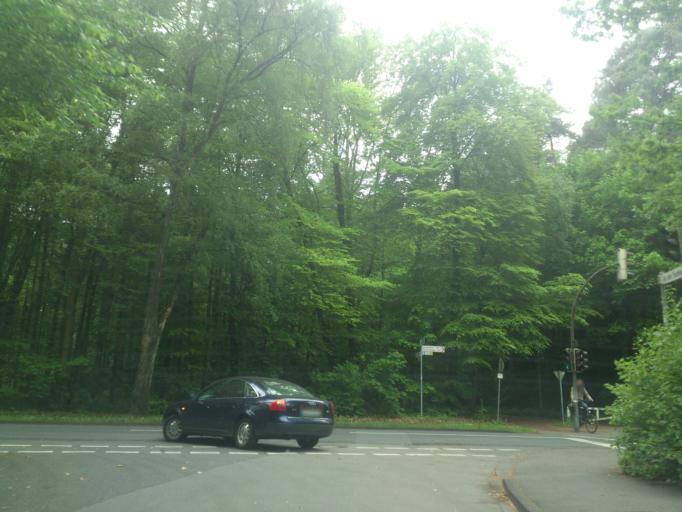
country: DE
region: North Rhine-Westphalia
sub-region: Regierungsbezirk Detmold
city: Paderborn
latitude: 51.7387
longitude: 8.7369
